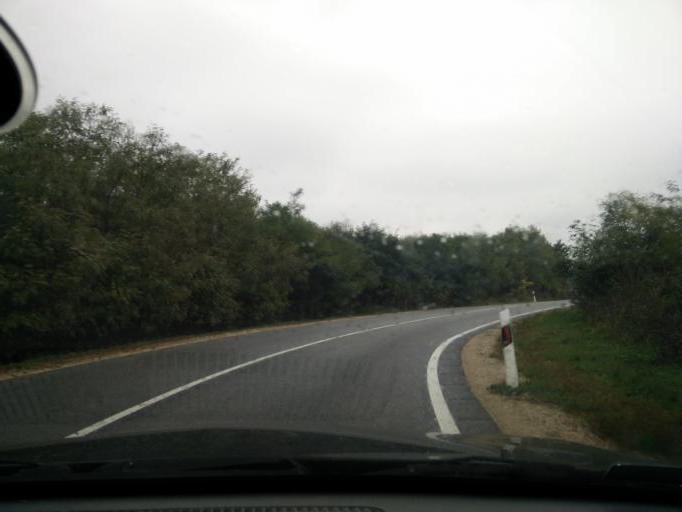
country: HU
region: Komarom-Esztergom
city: Bajna
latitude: 47.6365
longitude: 18.5565
